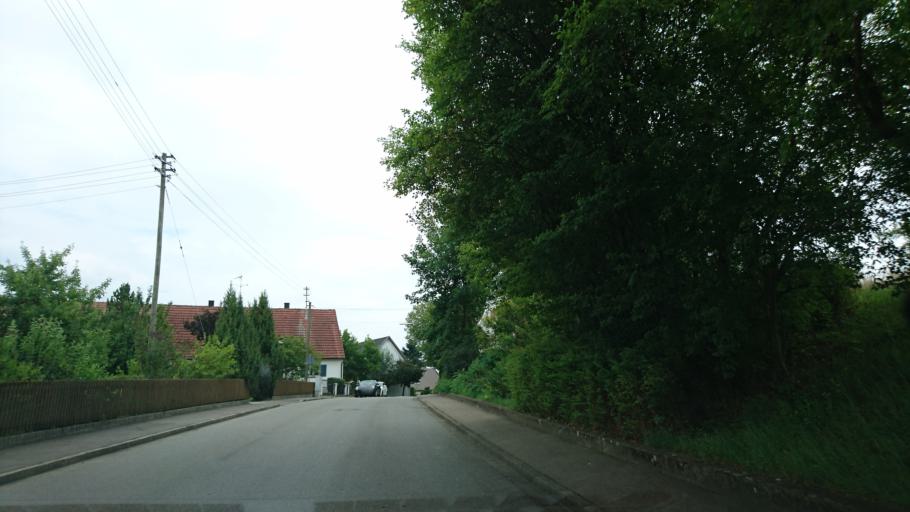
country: DE
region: Bavaria
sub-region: Swabia
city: Zusmarshausen
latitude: 48.3803
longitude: 10.5694
